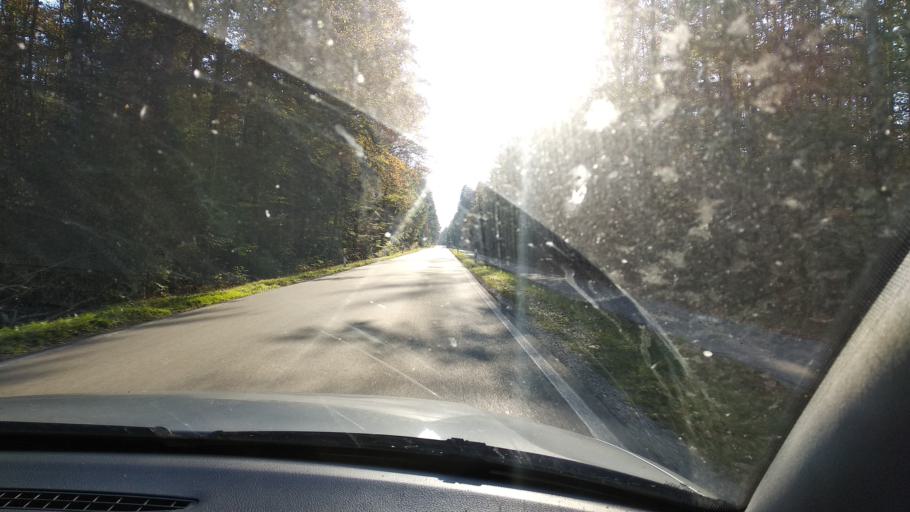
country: DE
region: Bavaria
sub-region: Upper Bavaria
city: Grasbrunn
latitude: 48.0475
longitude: 11.7613
